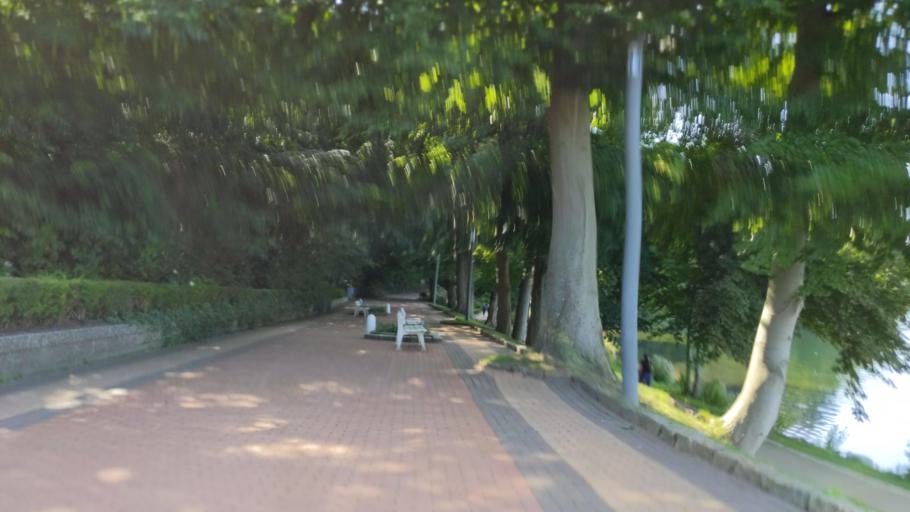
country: DE
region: Schleswig-Holstein
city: Malente
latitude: 54.1613
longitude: 10.5424
